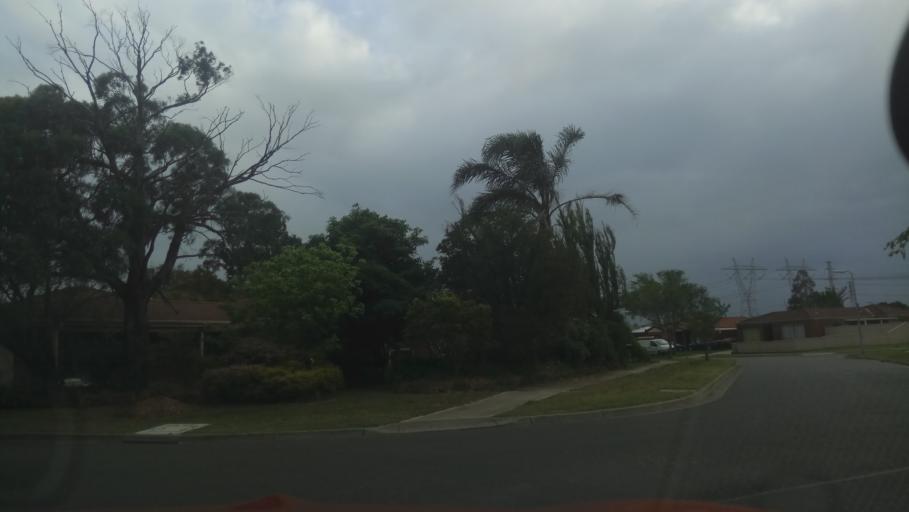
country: AU
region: Victoria
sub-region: Casey
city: Cranbourne North
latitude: -38.0699
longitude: 145.2668
